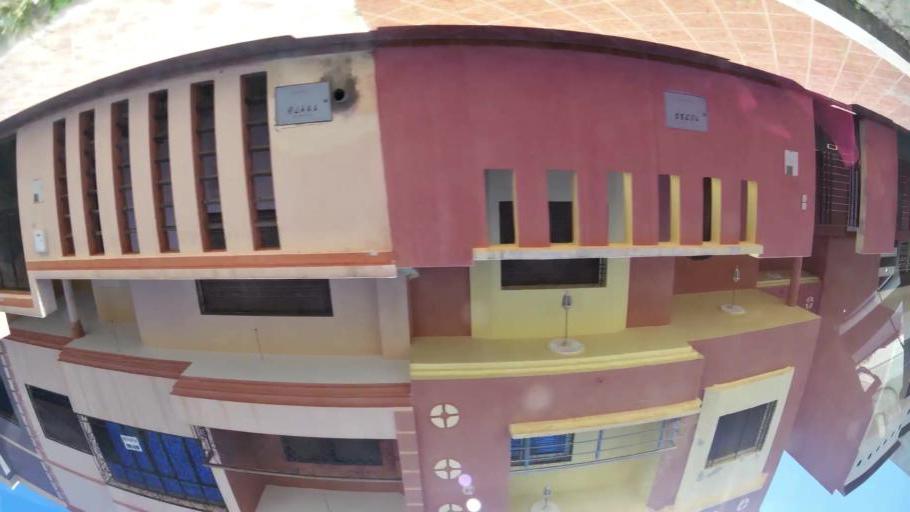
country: MA
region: Oriental
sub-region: Berkane-Taourirt
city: Madagh
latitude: 35.0856
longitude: -2.2439
